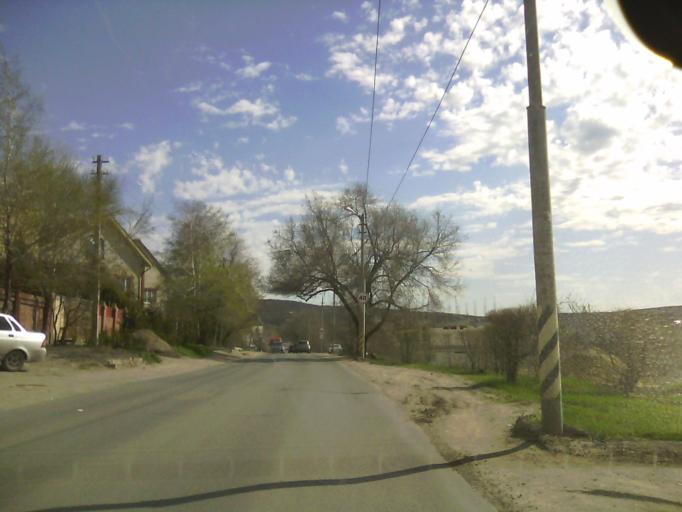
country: RU
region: Saratov
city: Sokolovyy
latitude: 51.5797
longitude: 45.8991
